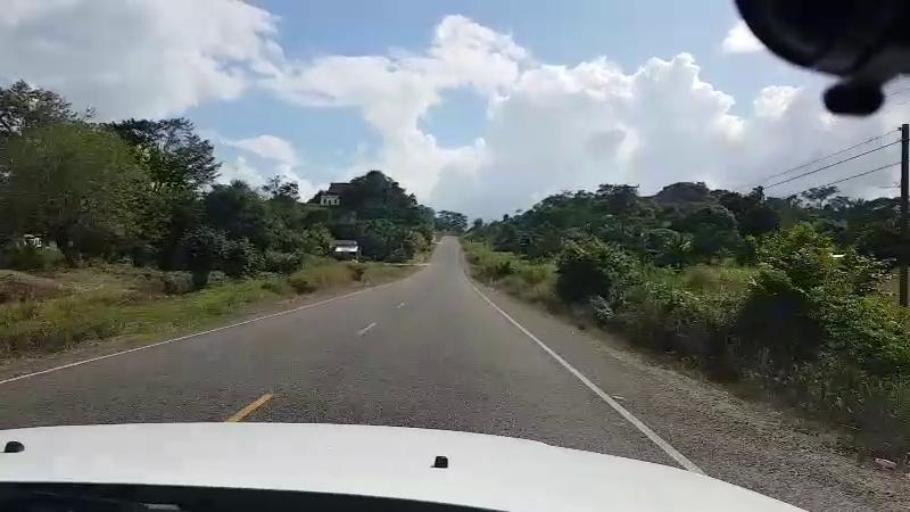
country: BZ
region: Cayo
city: Belmopan
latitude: 17.2350
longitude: -88.7805
